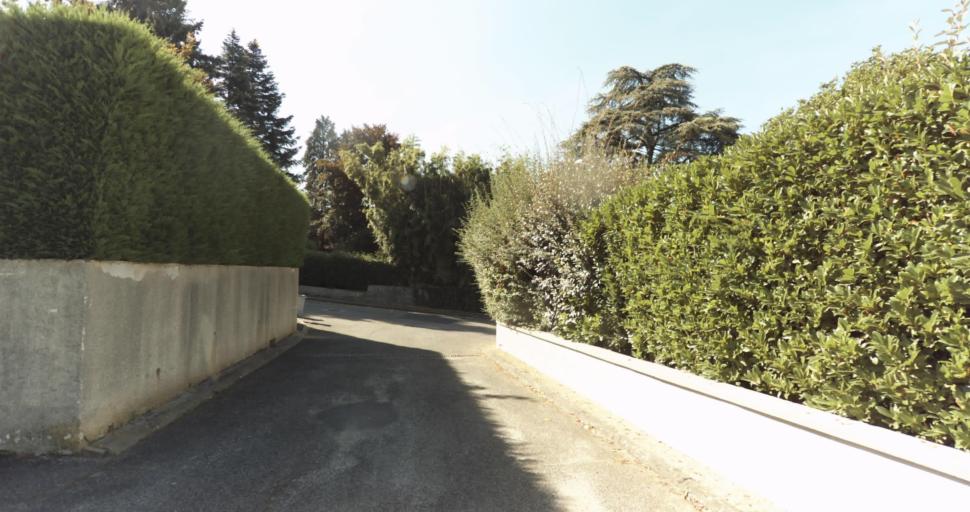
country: FR
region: Rhone-Alpes
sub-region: Departement du Rhone
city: Neuville-sur-Saone
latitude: 45.8749
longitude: 4.8484
